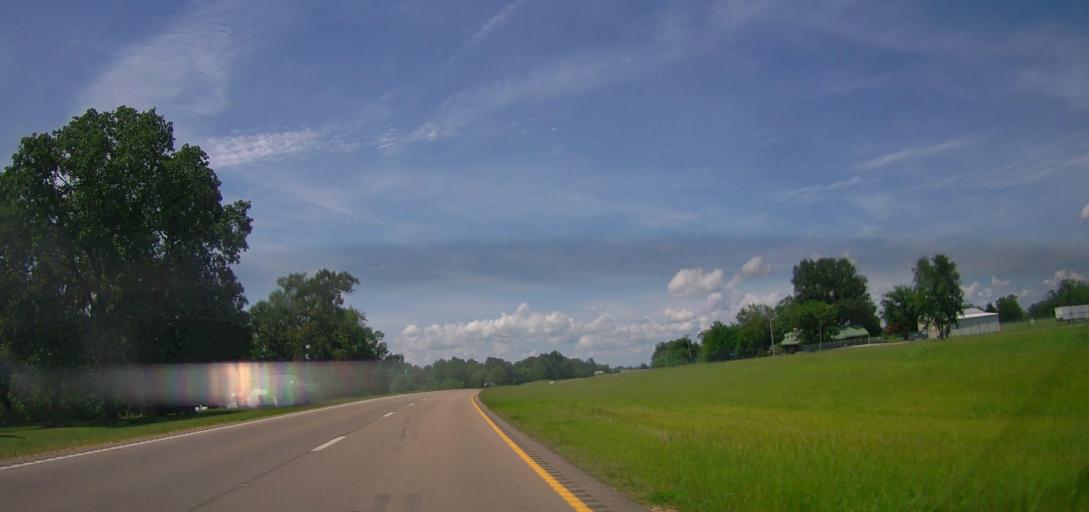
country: US
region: Mississippi
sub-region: Lee County
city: Nettleton
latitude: 33.9626
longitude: -88.6133
